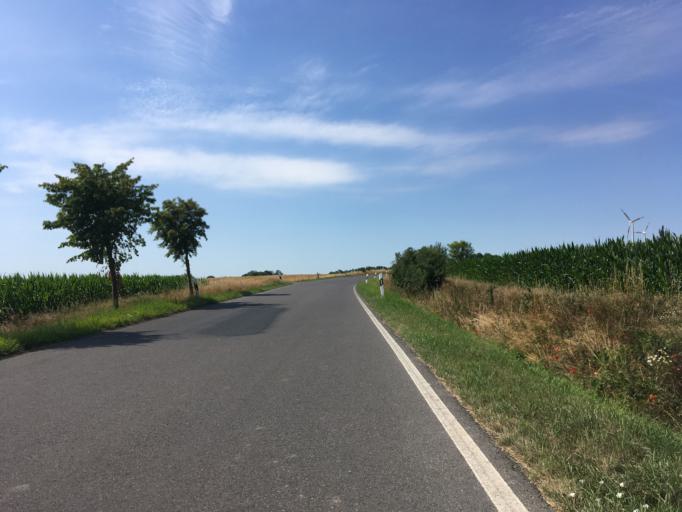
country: DE
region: Brandenburg
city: Gramzow
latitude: 53.2651
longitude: 14.0671
